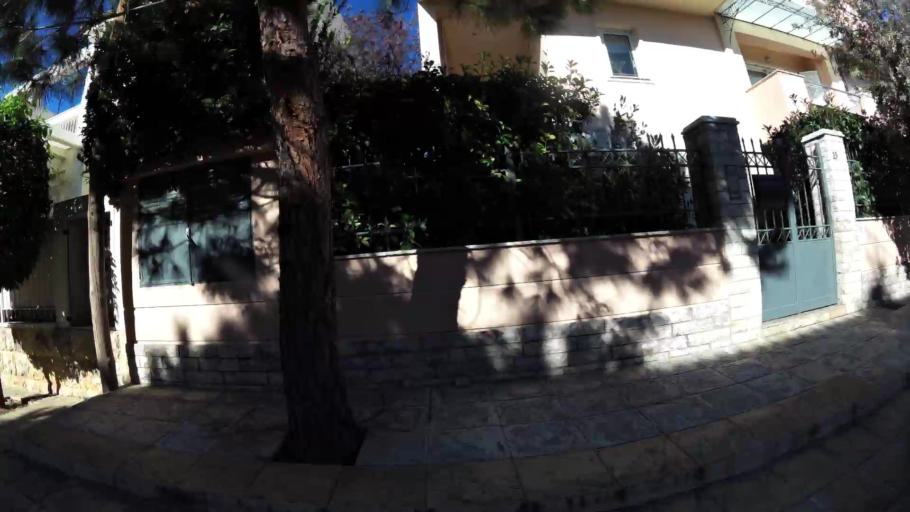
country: GR
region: Attica
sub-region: Nomarchia Athinas
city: Agia Paraskevi
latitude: 38.0260
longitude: 23.8359
